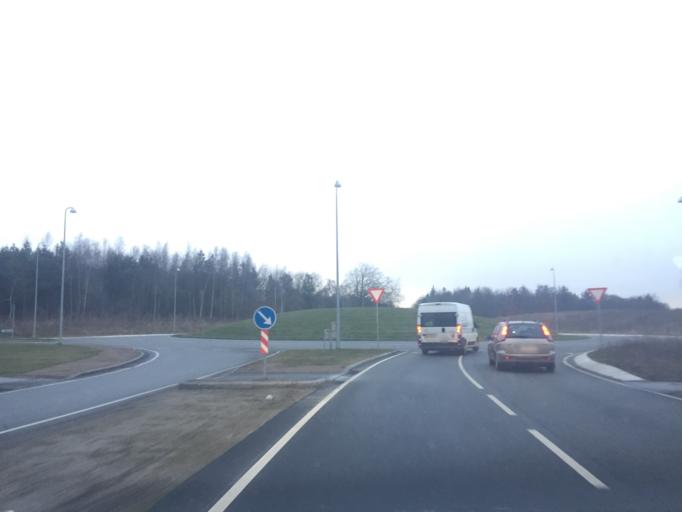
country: DK
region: Zealand
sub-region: Solrod Kommune
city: Solrod Strand
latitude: 55.5461
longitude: 12.2137
